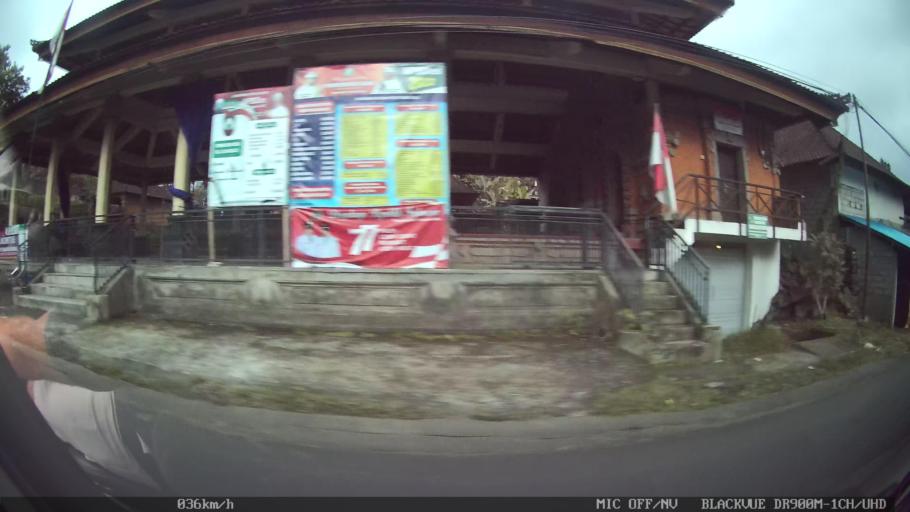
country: ID
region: Bali
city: Banjar Triwangsakeliki
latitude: -8.4509
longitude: 115.2619
